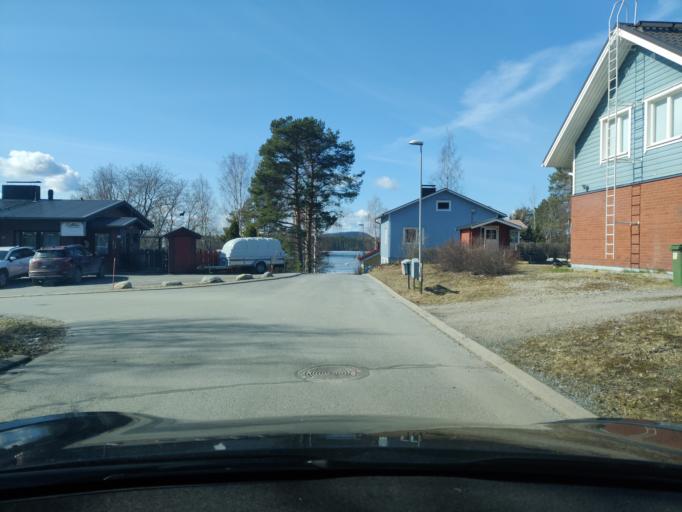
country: FI
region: Northern Savo
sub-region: Kuopio
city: Vehmersalmi
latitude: 62.7605
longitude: 28.0285
